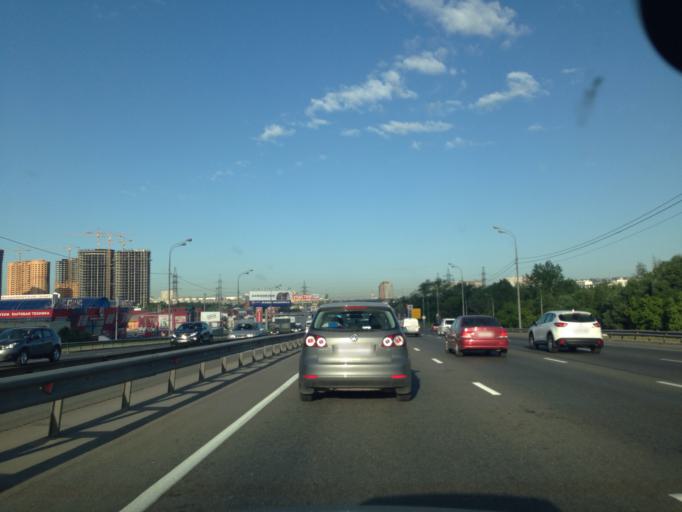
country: RU
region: Moskovskaya
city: Reutov
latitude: 55.7805
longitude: 37.8579
